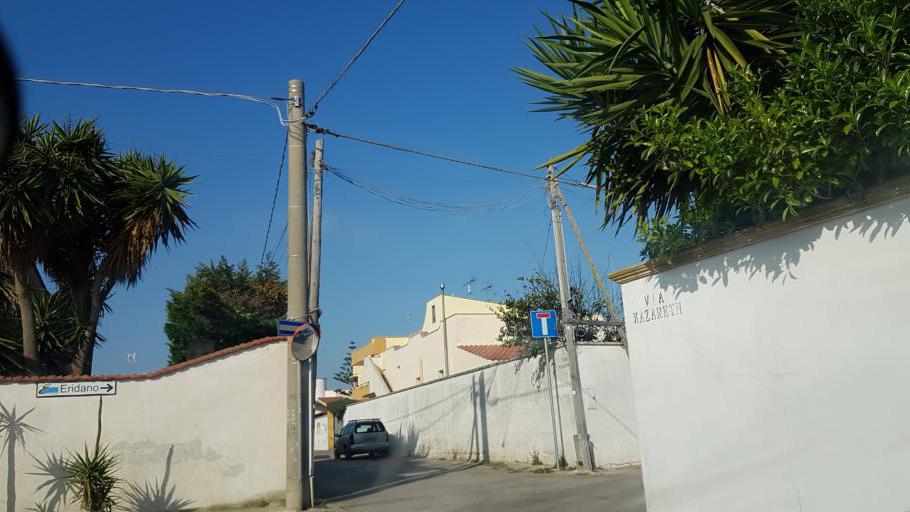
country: IT
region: Apulia
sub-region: Provincia di Brindisi
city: Materdomini
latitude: 40.6674
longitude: 17.9429
